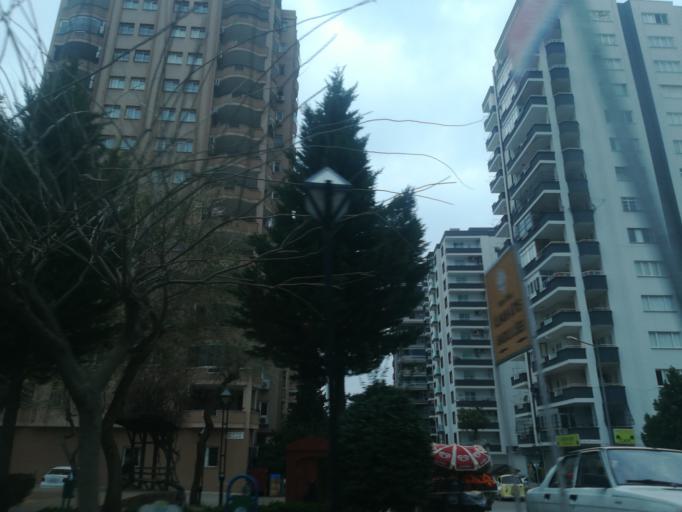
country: TR
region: Adana
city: Adana
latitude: 37.0296
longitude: 35.2986
